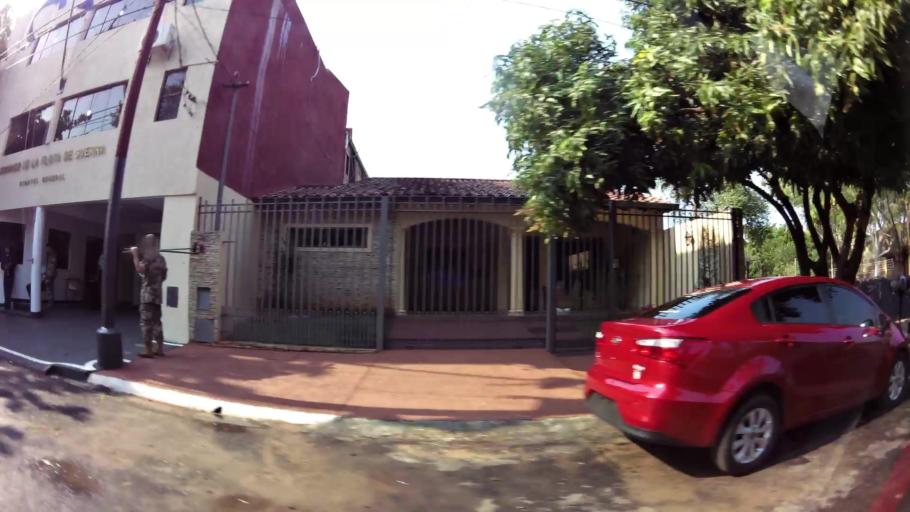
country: PY
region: Presidente Hayes
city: Nanawa
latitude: -25.2931
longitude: -57.6690
